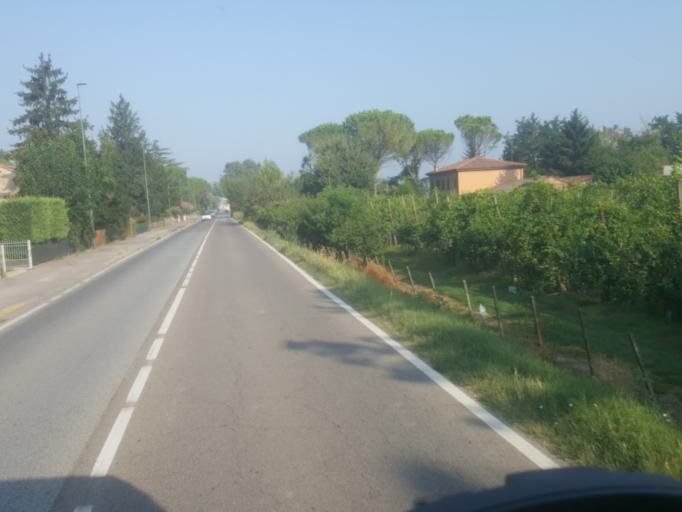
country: IT
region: Emilia-Romagna
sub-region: Provincia di Ravenna
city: Mezzano
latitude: 44.4618
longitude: 12.0954
